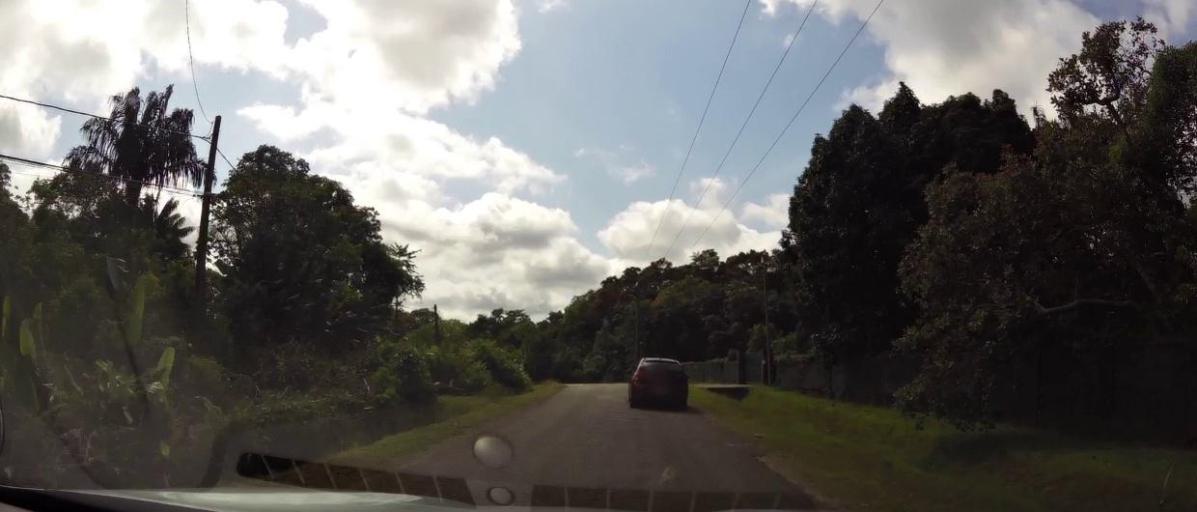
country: GF
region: Guyane
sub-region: Guyane
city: Matoury
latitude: 4.8302
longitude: -52.3125
